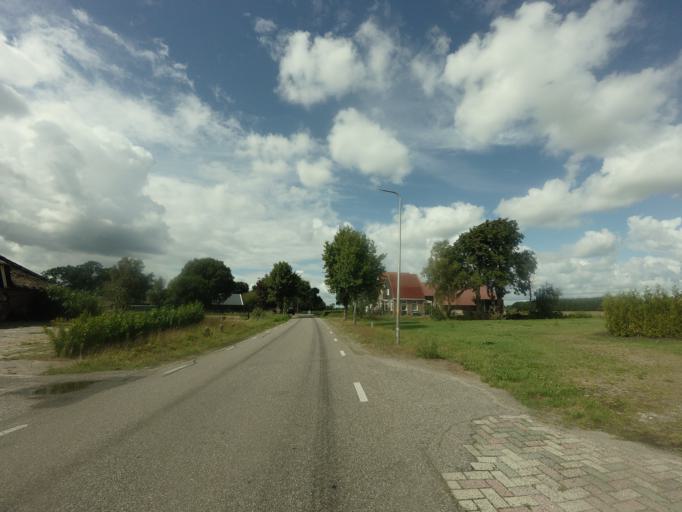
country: NL
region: Overijssel
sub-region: Gemeente Staphorst
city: Staphorst
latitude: 52.6735
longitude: 6.2449
